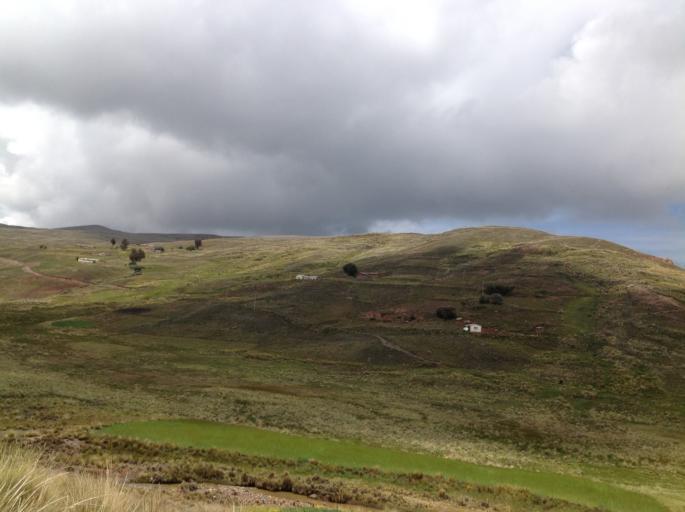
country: BO
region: La Paz
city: Yumani
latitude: -15.7675
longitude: -68.9904
